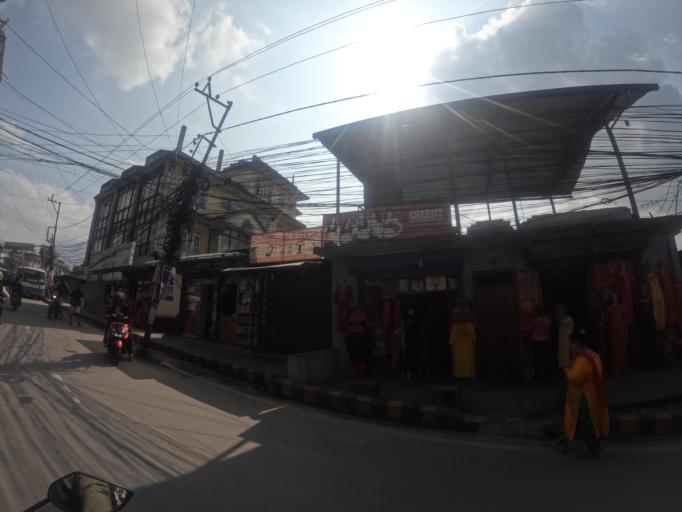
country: NP
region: Central Region
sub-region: Bagmati Zone
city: Patan
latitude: 27.6739
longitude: 85.3651
